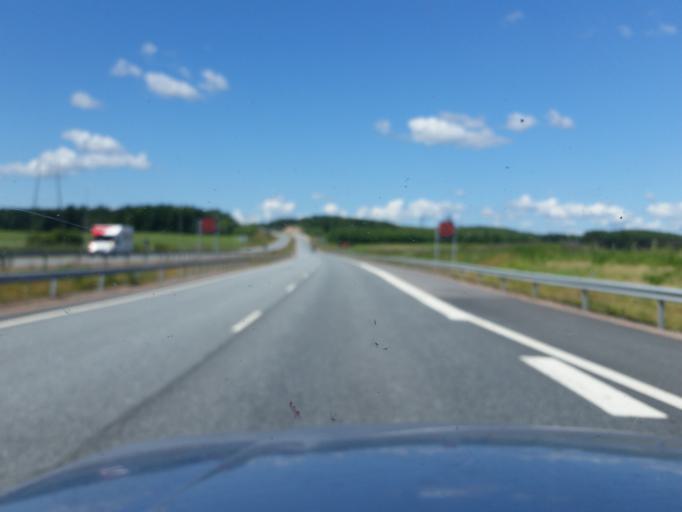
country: FI
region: Varsinais-Suomi
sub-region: Salo
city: Kiikala
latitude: 60.3904
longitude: 23.5786
